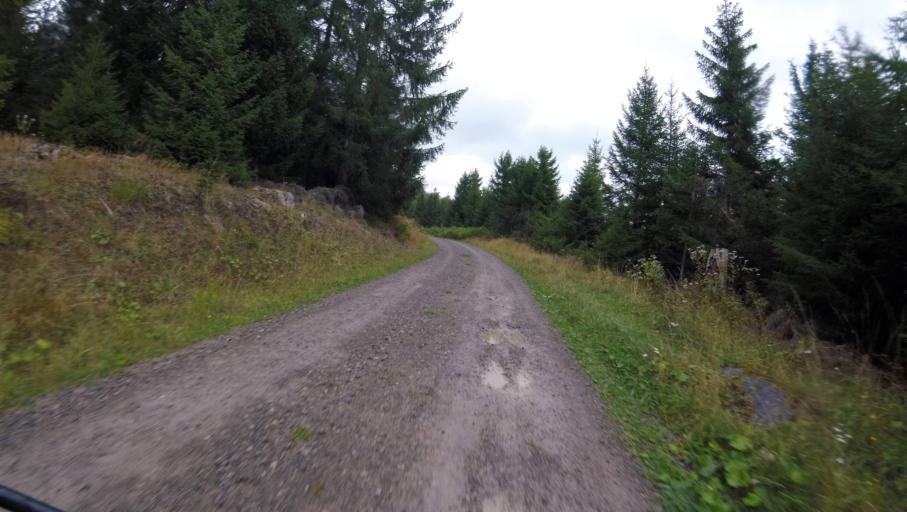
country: DE
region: Baden-Wuerttemberg
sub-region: Karlsruhe Region
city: Forbach
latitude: 48.6820
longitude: 8.4170
